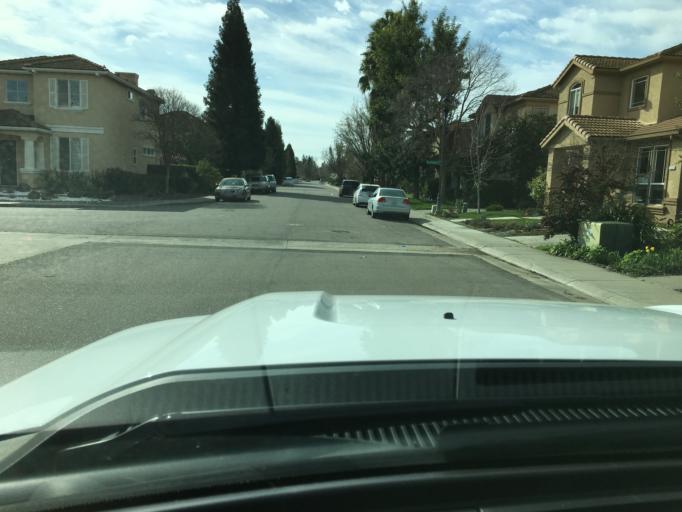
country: US
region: California
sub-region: Yolo County
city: Davis
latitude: 38.5580
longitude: -121.7753
